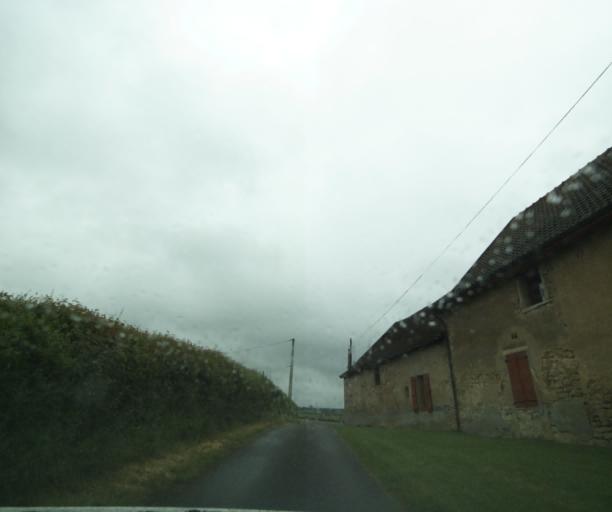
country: FR
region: Bourgogne
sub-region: Departement de Saone-et-Loire
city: Palinges
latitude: 46.4905
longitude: 4.1952
